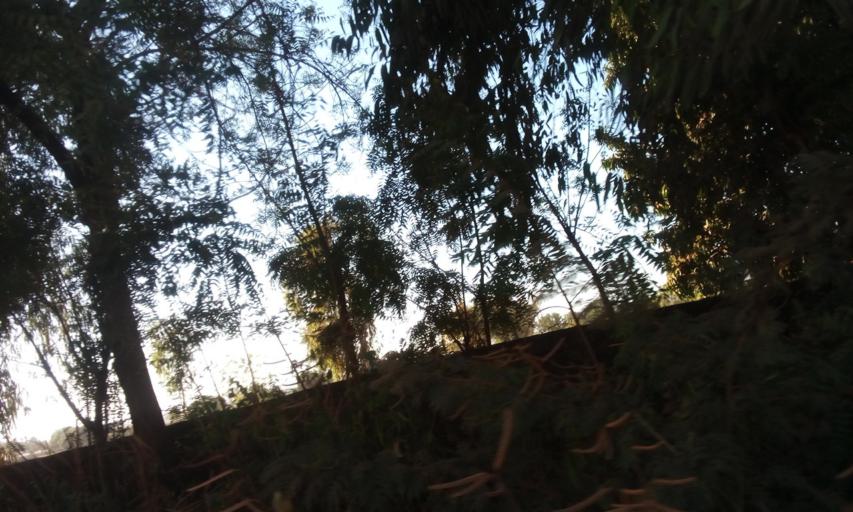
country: ML
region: Bamako
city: Bamako
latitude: 12.6431
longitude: -7.9056
